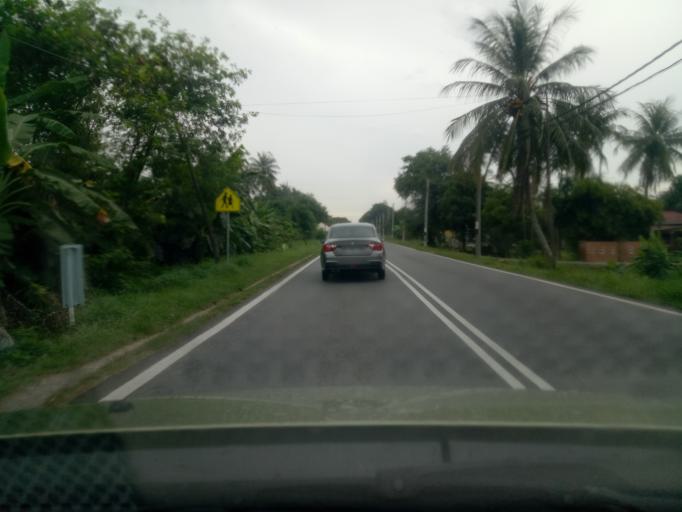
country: MY
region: Kedah
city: Gurun
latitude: 5.9701
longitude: 100.4218
